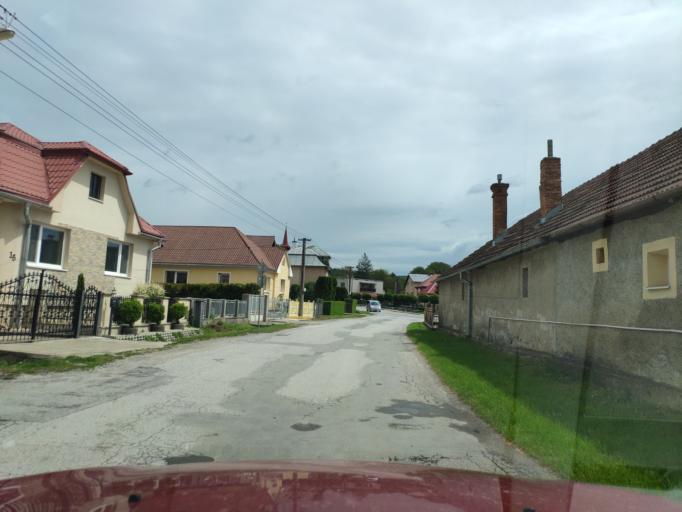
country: SK
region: Kosicky
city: Kosice
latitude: 48.7320
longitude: 21.3424
